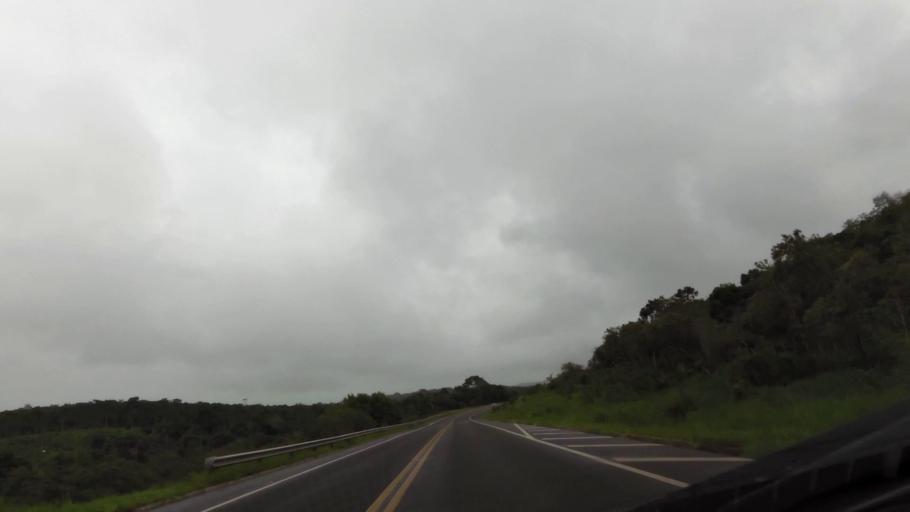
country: BR
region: Espirito Santo
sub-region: Guarapari
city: Guarapari
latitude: -20.7200
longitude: -40.5742
